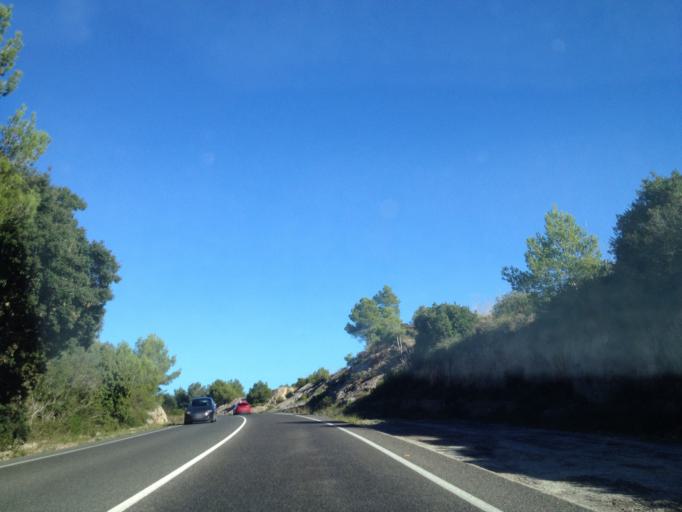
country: ES
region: Balearic Islands
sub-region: Illes Balears
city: Sant Llorenc des Cardassar
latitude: 39.6426
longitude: 3.3132
